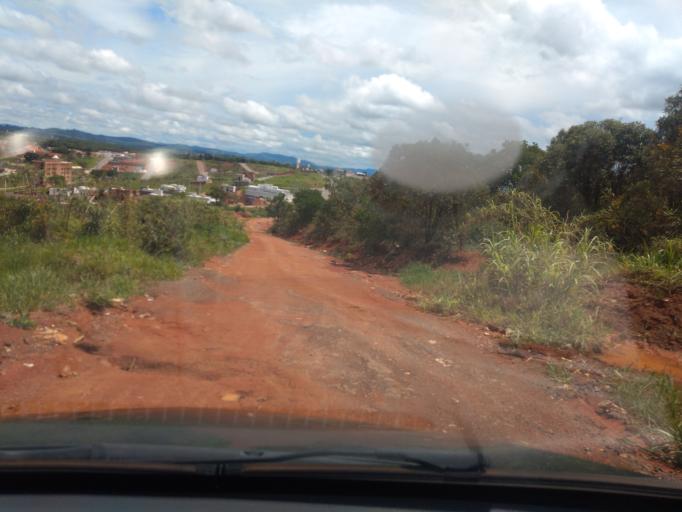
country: BR
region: Minas Gerais
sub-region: Tres Coracoes
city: Tres Coracoes
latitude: -21.6751
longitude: -45.2780
